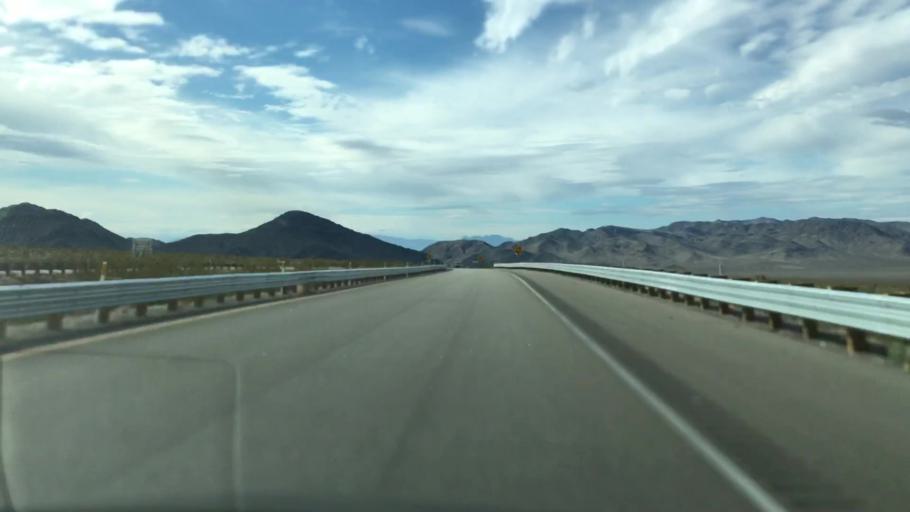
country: US
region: Nevada
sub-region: Nye County
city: Pahrump
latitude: 36.5959
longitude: -116.0095
